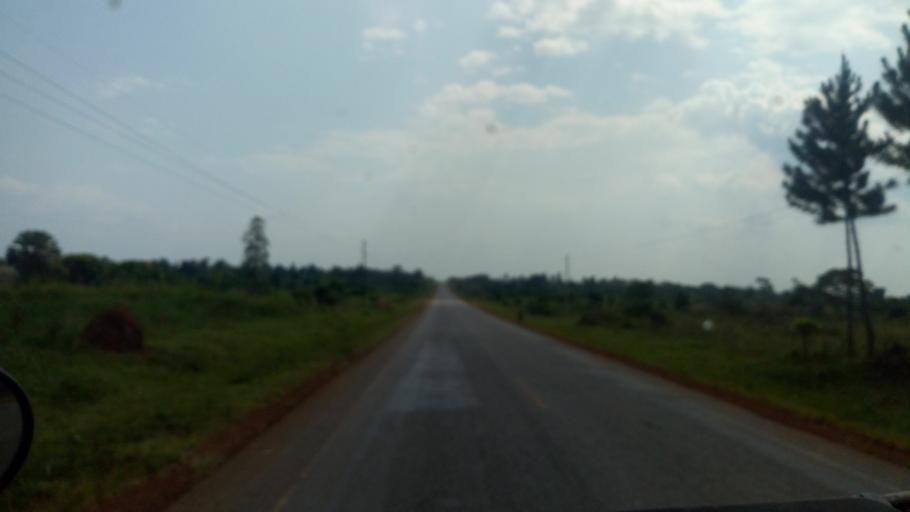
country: UG
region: Northern Region
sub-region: Oyam District
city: Oyam
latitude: 2.2180
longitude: 32.3972
